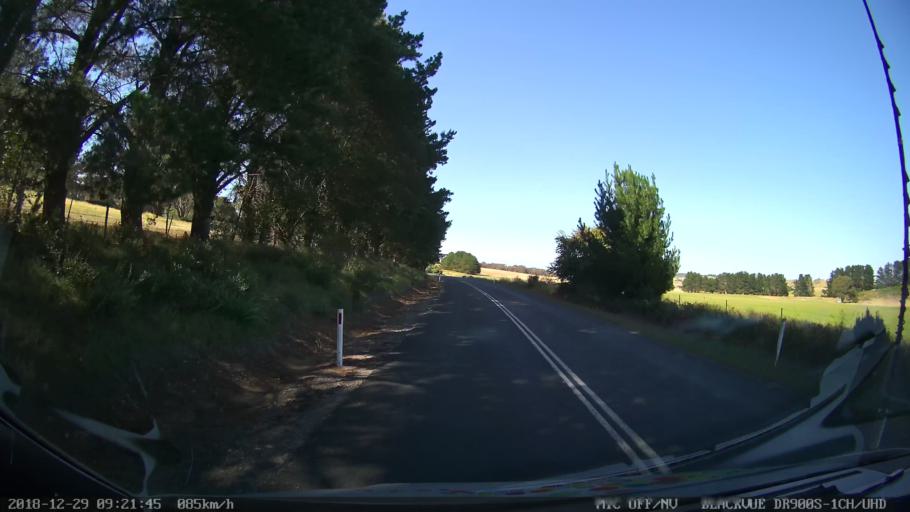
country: AU
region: New South Wales
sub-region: Upper Lachlan Shire
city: Crookwell
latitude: -34.5049
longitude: 149.4112
